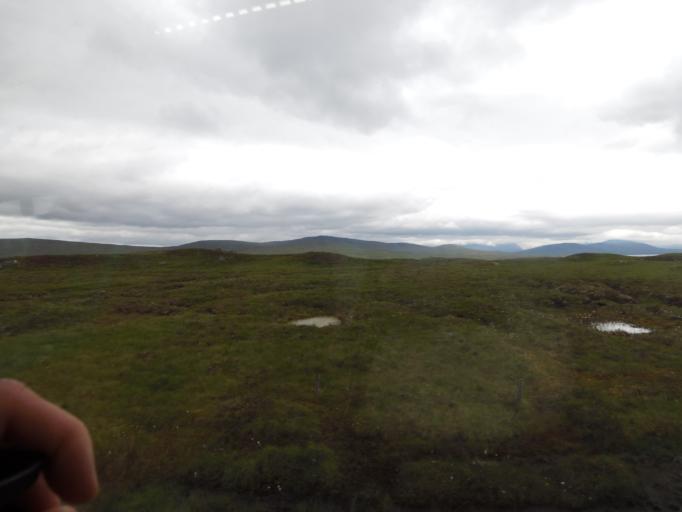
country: GB
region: Scotland
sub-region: Highland
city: Spean Bridge
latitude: 56.7256
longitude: -4.6371
